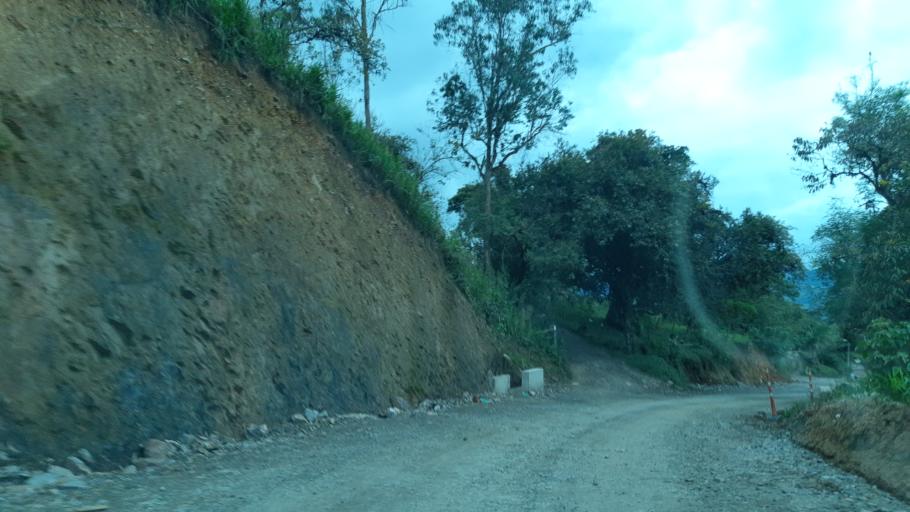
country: CO
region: Boyaca
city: Garagoa
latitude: 5.0850
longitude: -73.3546
